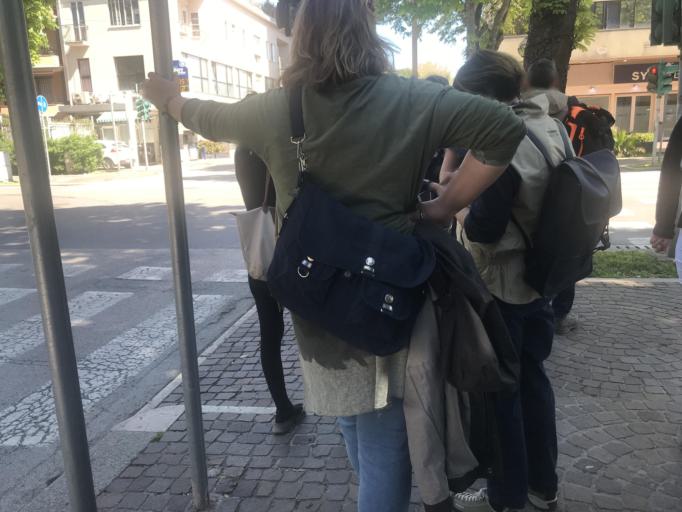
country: IT
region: Emilia-Romagna
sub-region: Provincia di Rimini
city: Rimini
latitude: 44.0669
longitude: 12.5715
